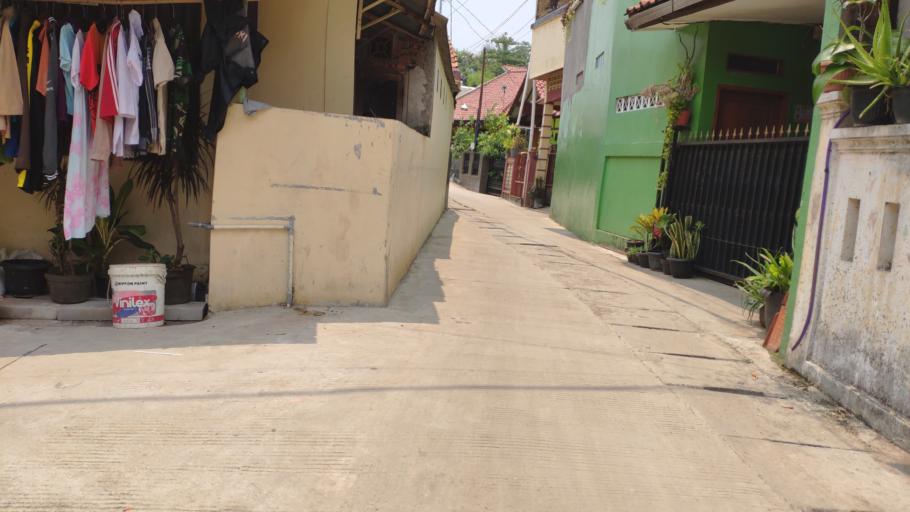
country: ID
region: West Java
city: Depok
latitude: -6.3520
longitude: 106.8048
